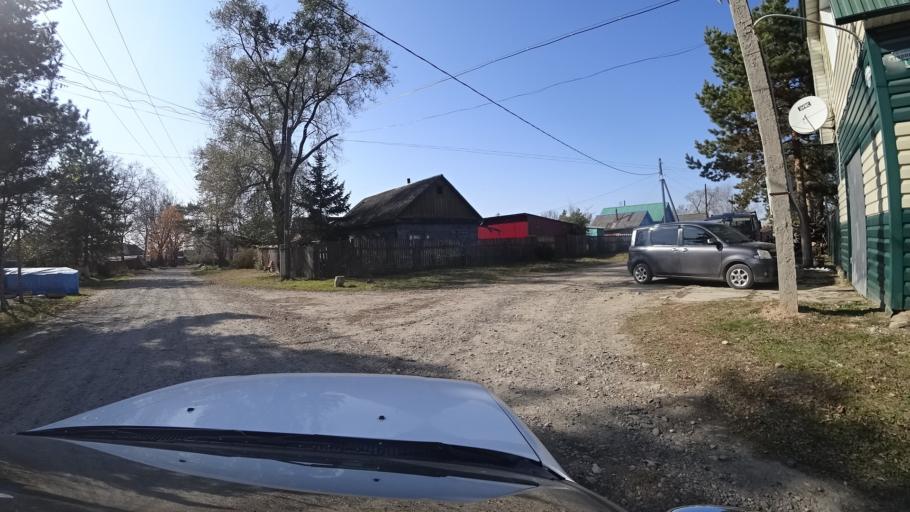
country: RU
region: Primorskiy
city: Dal'nerechensk
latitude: 45.9286
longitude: 133.7513
